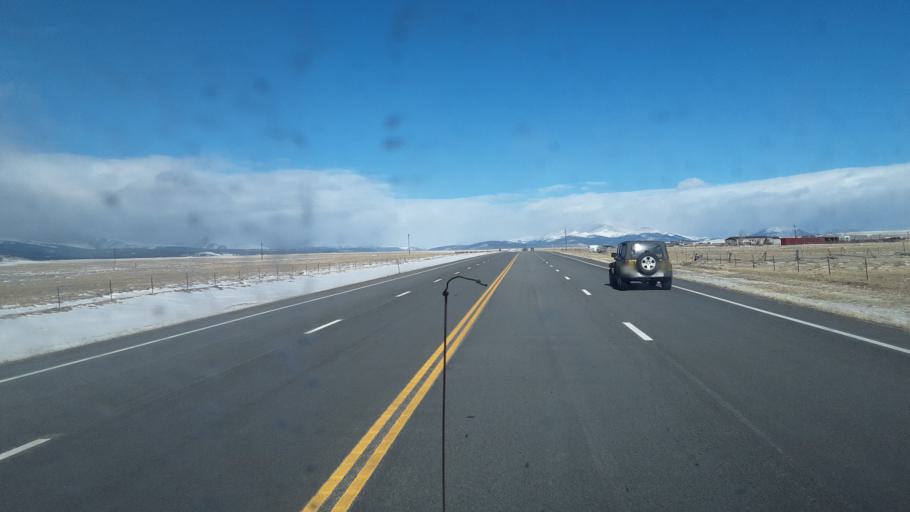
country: US
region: Colorado
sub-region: Park County
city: Fairplay
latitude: 39.1184
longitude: -105.9925
